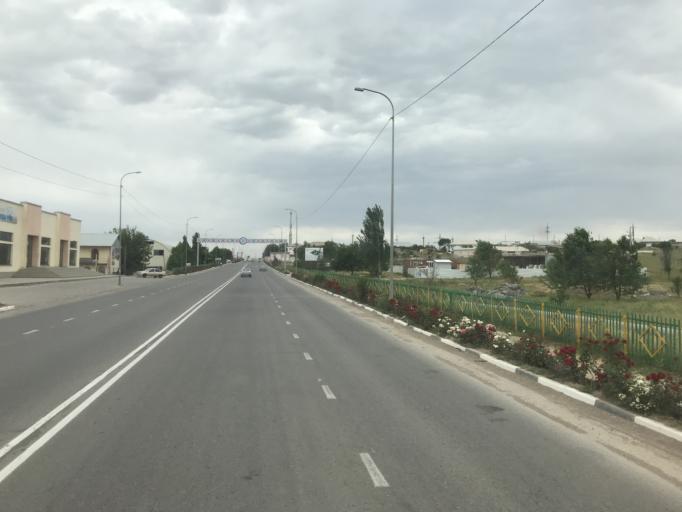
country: KZ
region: Ongtustik Qazaqstan
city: Saryaghash
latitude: 41.4723
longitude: 69.1795
